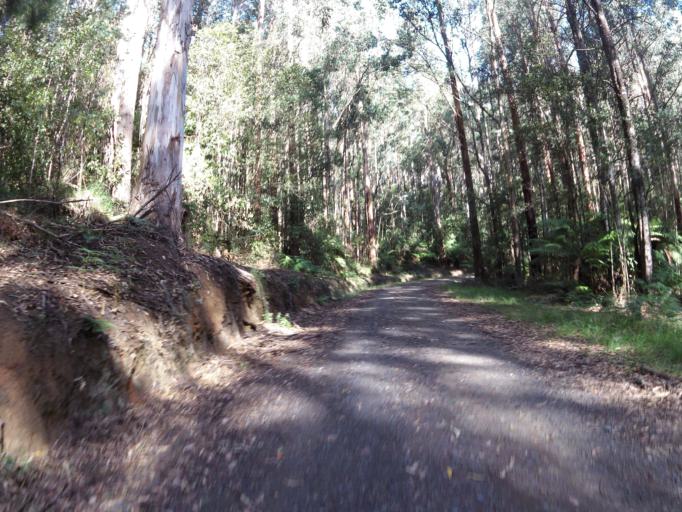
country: AU
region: Victoria
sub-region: Yarra Ranges
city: Millgrove
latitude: -37.8488
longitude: 145.7987
